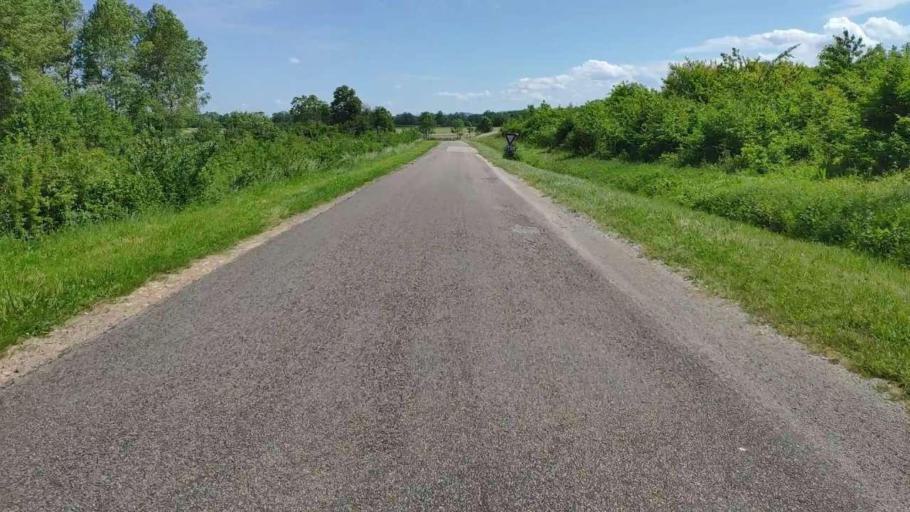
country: FR
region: Franche-Comte
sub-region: Departement du Jura
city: Bletterans
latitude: 46.7167
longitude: 5.4415
